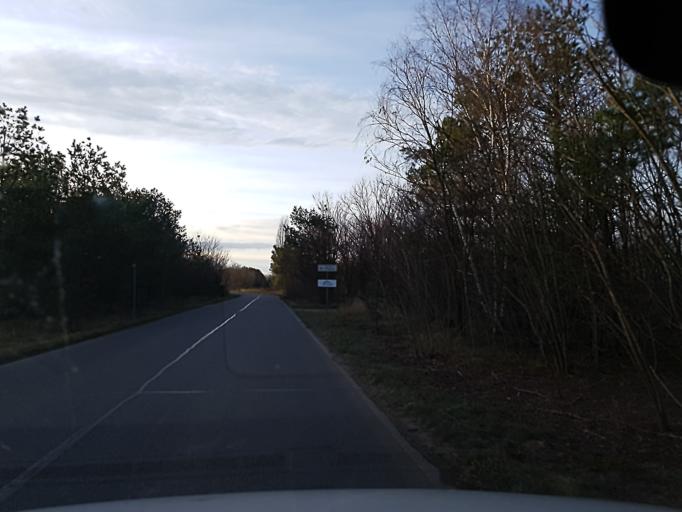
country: DE
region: Brandenburg
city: Finsterwalde
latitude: 51.6041
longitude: 13.7516
